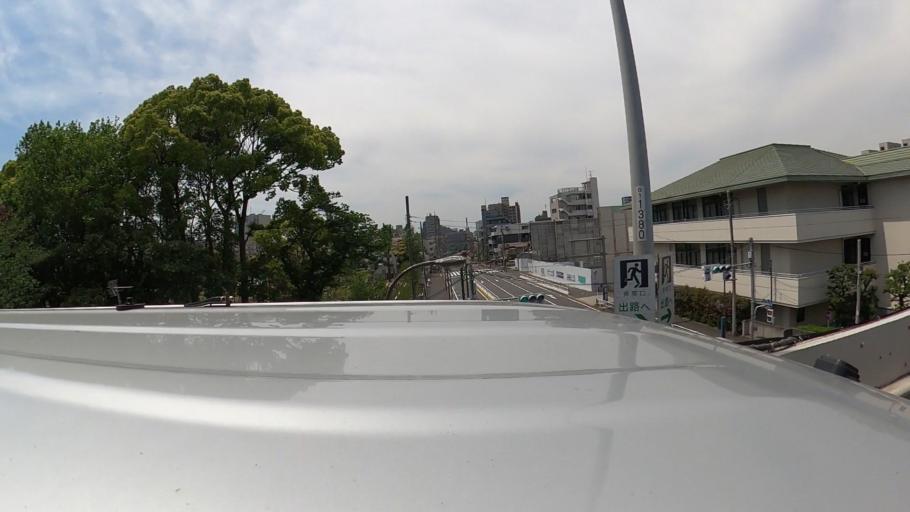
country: JP
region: Kanagawa
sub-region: Kawasaki-shi
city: Kawasaki
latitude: 35.5959
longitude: 139.7420
